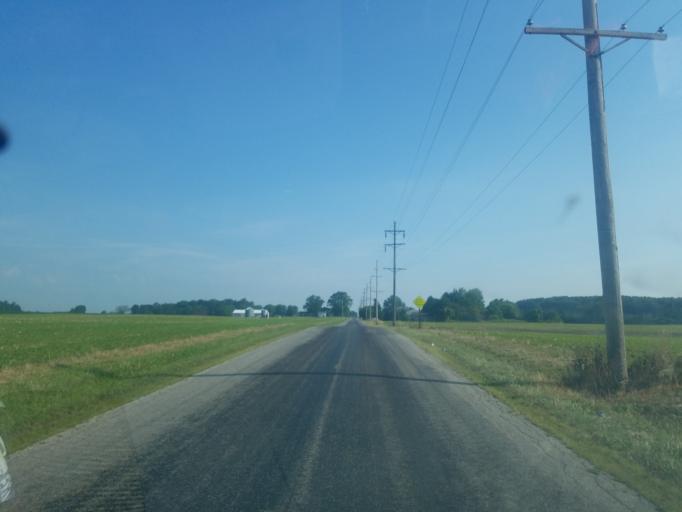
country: US
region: Ohio
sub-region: Huron County
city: Plymouth
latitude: 40.9380
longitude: -82.6859
